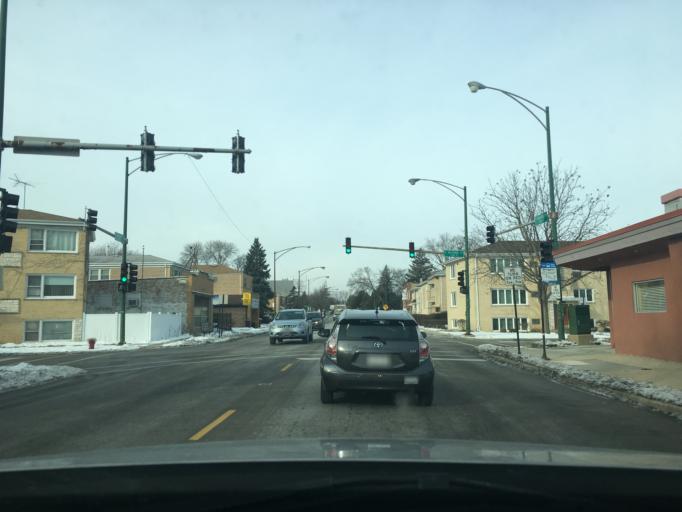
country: US
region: Illinois
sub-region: Cook County
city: Harwood Heights
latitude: 41.9778
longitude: -87.7924
